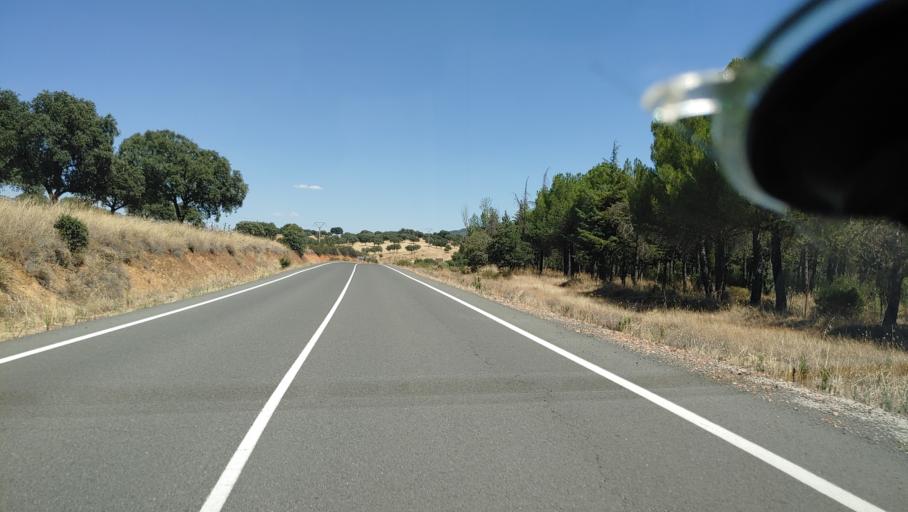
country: ES
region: Castille-La Mancha
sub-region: Provincia de Ciudad Real
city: Almaden
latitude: 38.8306
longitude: -4.7075
